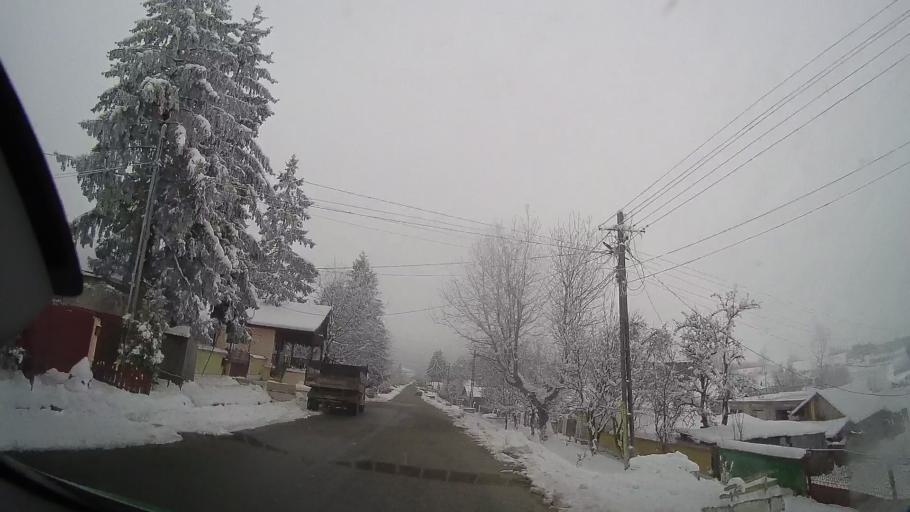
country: RO
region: Neamt
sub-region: Comuna Valea Ursului
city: Valea Ursului
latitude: 46.8533
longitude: 27.0533
